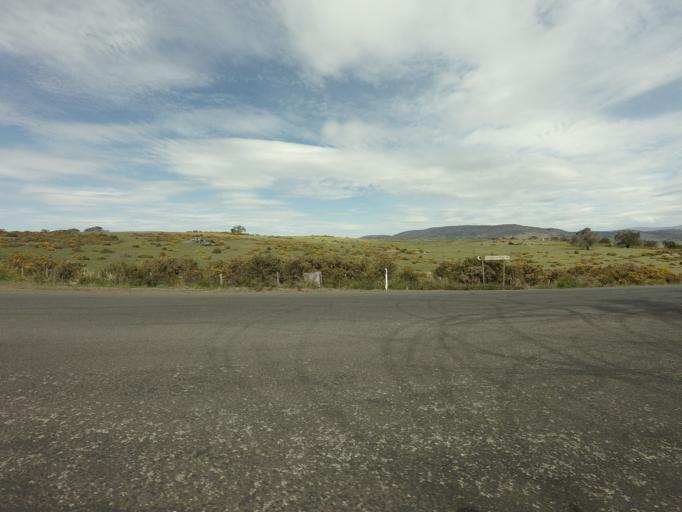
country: AU
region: Tasmania
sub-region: Northern Midlands
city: Evandale
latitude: -41.8948
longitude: 147.4107
